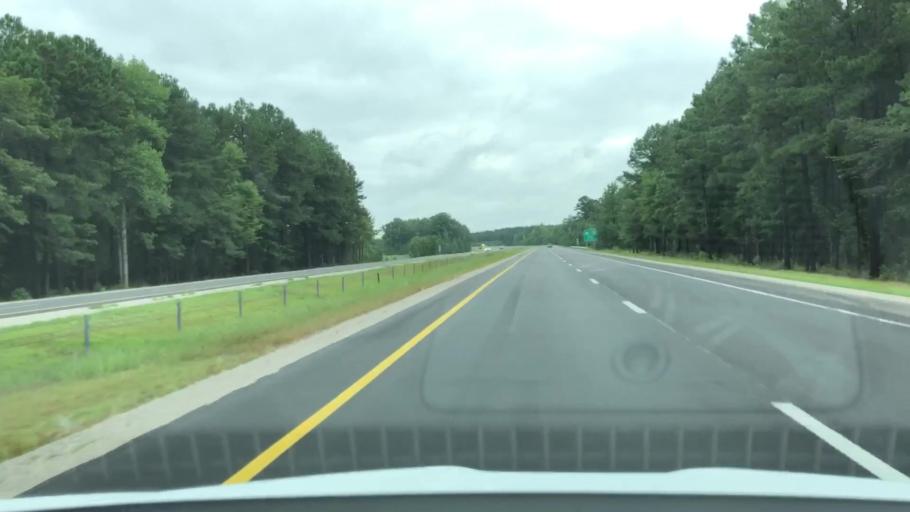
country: US
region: North Carolina
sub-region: Wilson County
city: Lucama
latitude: 35.6550
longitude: -77.9587
